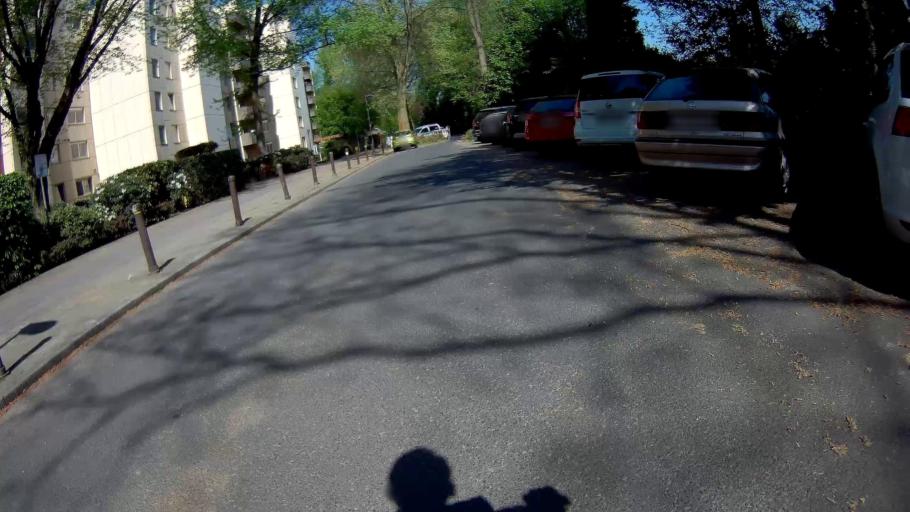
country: DE
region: North Rhine-Westphalia
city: Marl
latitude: 51.5844
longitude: 7.0625
